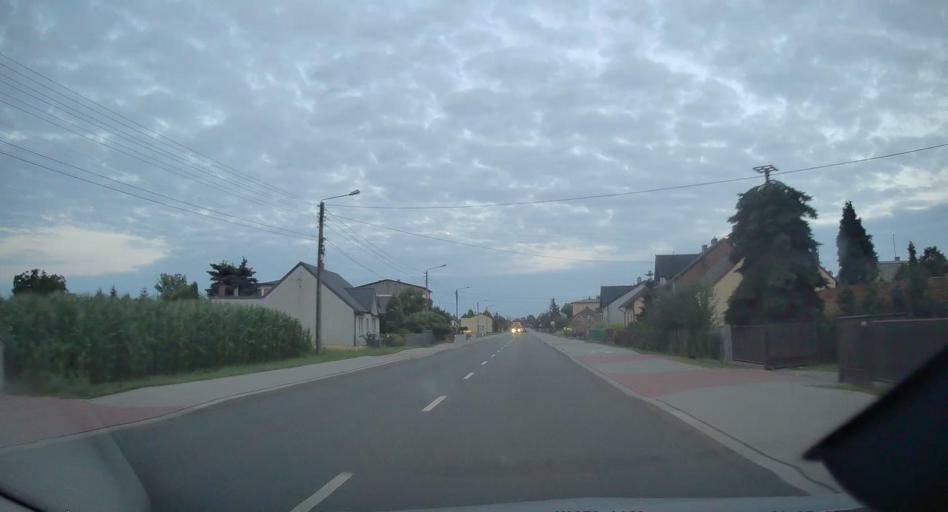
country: PL
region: Silesian Voivodeship
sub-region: Powiat klobucki
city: Starokrzepice
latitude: 51.0104
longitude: 18.6568
